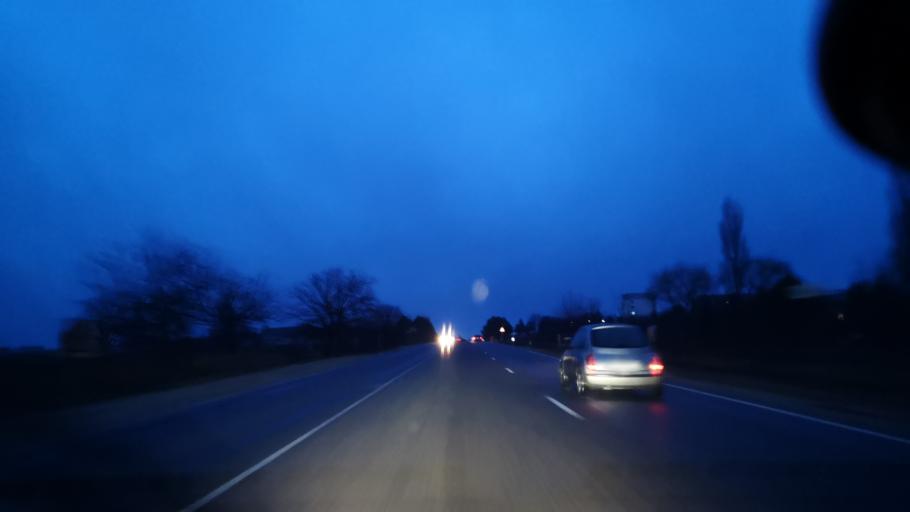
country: MD
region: Orhei
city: Orhei
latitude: 47.3978
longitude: 28.8030
